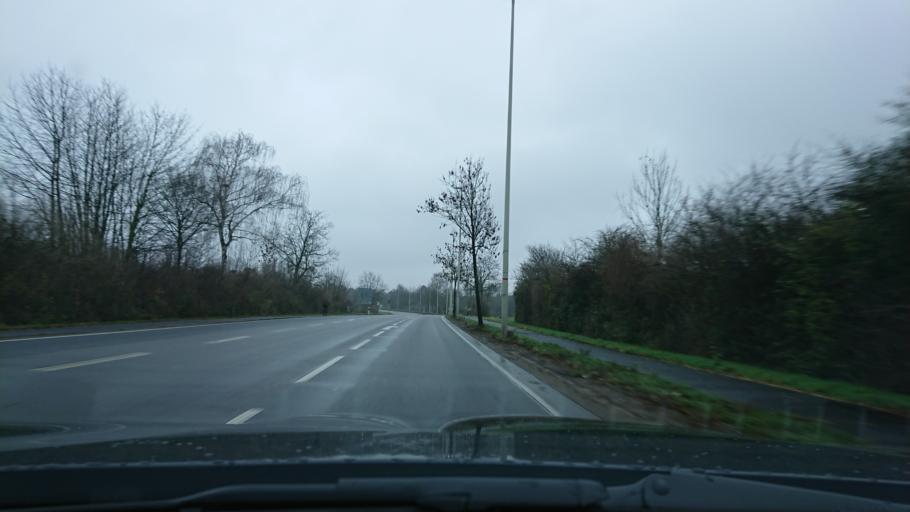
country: DE
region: North Rhine-Westphalia
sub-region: Regierungsbezirk Koln
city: Bonn
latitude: 50.7572
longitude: 7.1167
